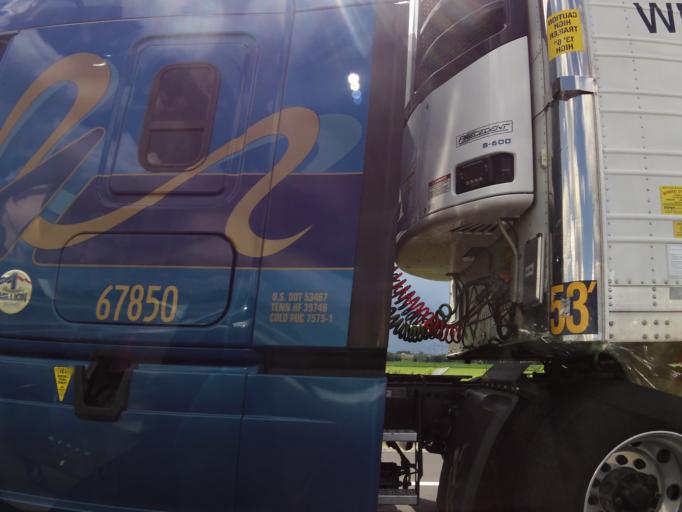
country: US
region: Iowa
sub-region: Johnson County
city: University Heights
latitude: 41.5709
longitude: -91.5453
